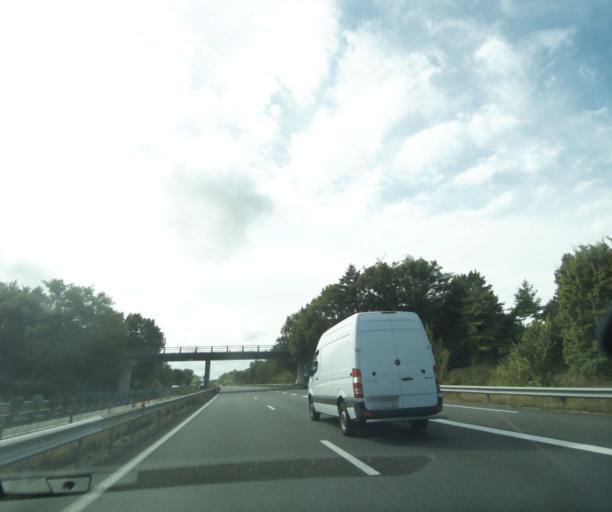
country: FR
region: Poitou-Charentes
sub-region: Departement de la Charente-Maritime
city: Pons
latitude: 45.5769
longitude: -0.5998
